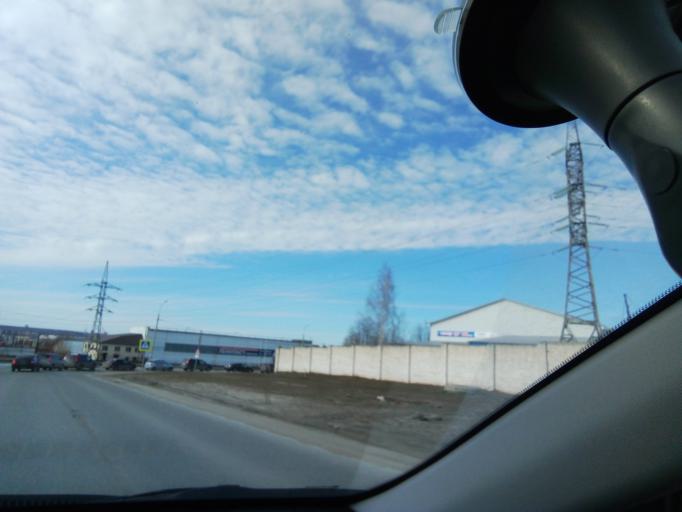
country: RU
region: Chuvashia
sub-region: Cheboksarskiy Rayon
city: Cheboksary
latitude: 56.1000
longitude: 47.2531
